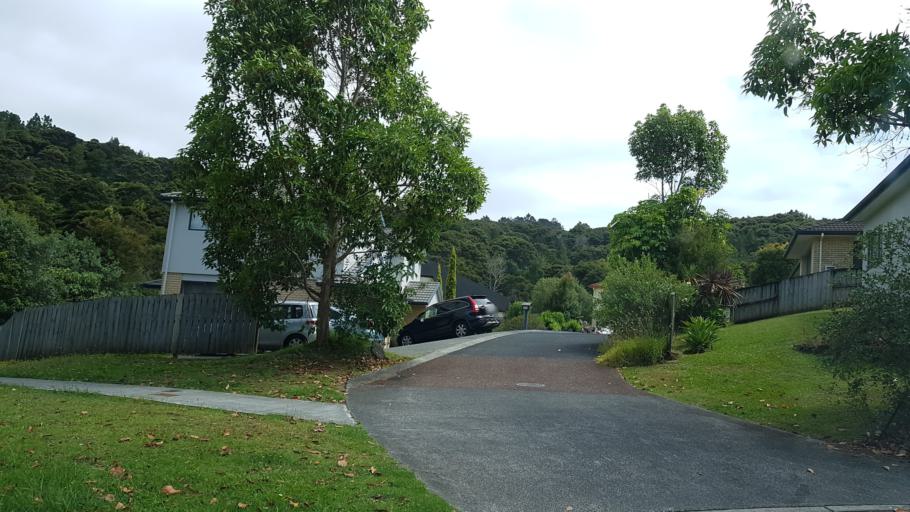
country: NZ
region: Auckland
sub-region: Auckland
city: North Shore
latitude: -36.7701
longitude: 174.7069
